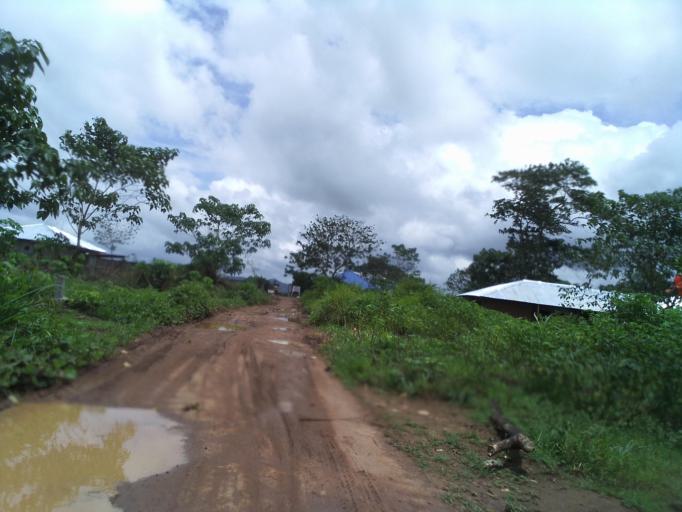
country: SL
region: Eastern Province
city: Kenema
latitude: 7.8227
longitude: -11.1807
